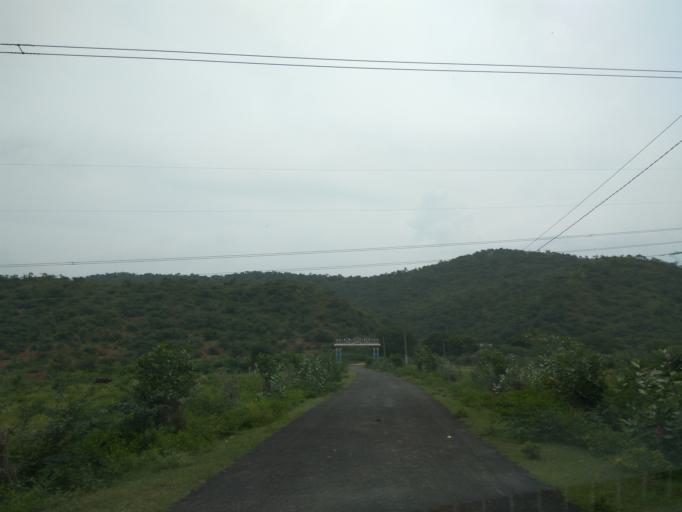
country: IN
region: Andhra Pradesh
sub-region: Prakasam
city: Cumbum
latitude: 15.4445
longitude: 79.0810
